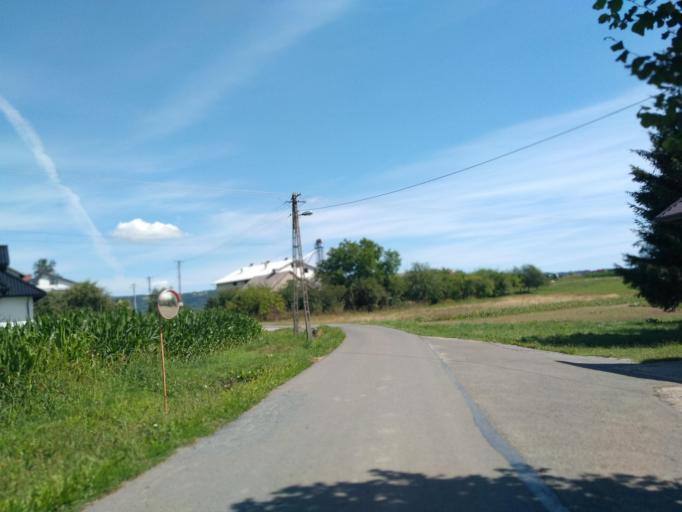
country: PL
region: Subcarpathian Voivodeship
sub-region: Powiat krosnienski
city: Kroscienko Wyzne
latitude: 49.7032
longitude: 21.8325
